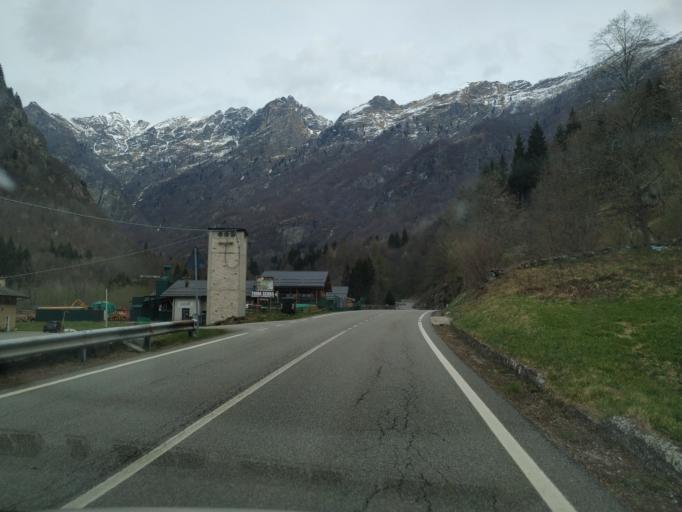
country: IT
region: Piedmont
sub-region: Provincia di Vercelli
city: Campertogno
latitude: 45.8055
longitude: 8.0332
